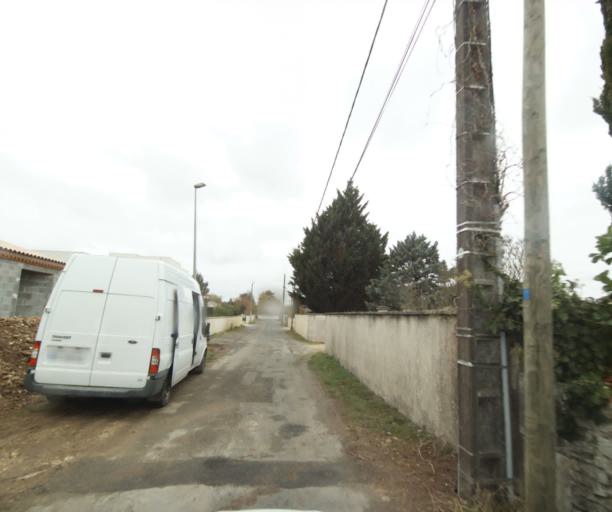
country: FR
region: Poitou-Charentes
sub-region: Departement de la Charente-Maritime
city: Bussac-sur-Charente
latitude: 45.7688
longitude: -0.6326
